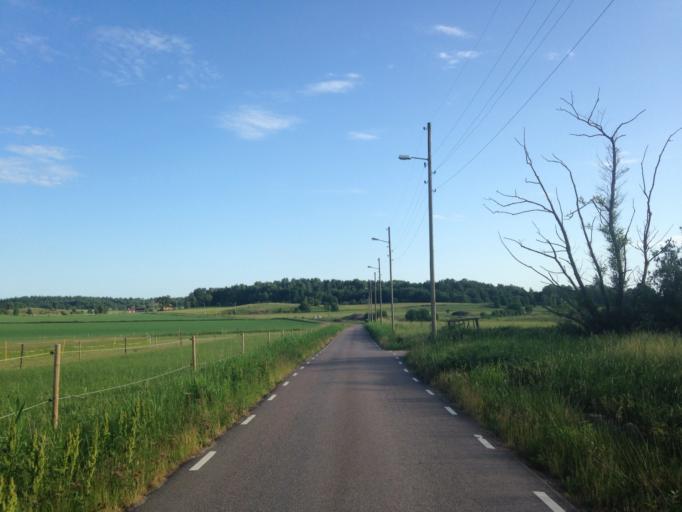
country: SE
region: Vaestra Goetaland
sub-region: Goteborg
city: Majorna
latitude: 57.7998
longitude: 11.8869
